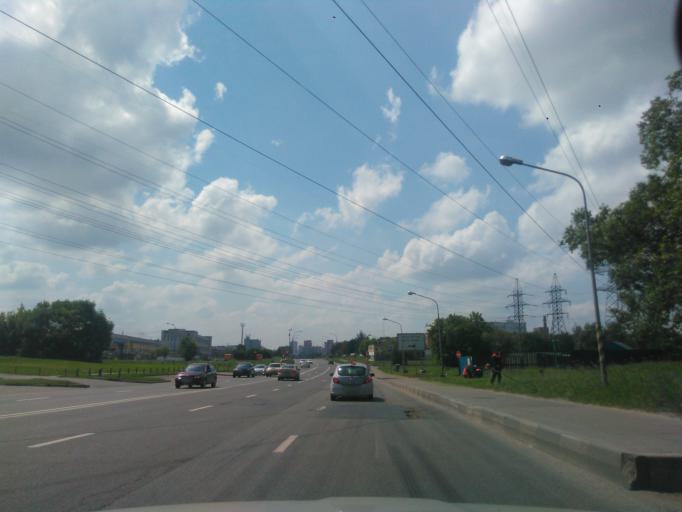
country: RU
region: Moscow
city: Businovo
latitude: 55.8873
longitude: 37.5076
